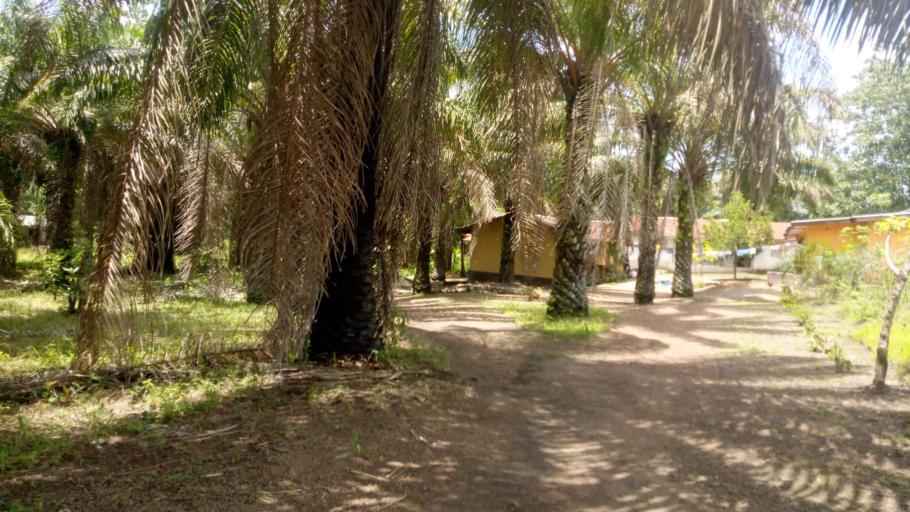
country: SL
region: Northern Province
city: Magburaka
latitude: 8.7129
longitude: -11.9530
